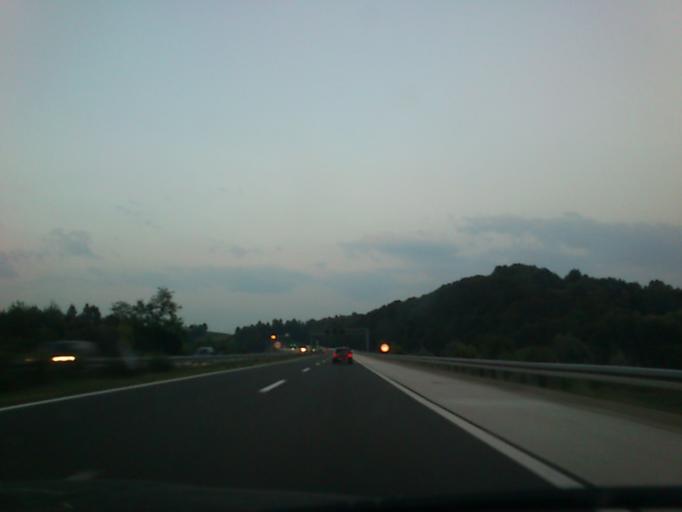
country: HR
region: Karlovacka
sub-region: Grad Karlovac
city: Karlovac
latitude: 45.5007
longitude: 15.4542
